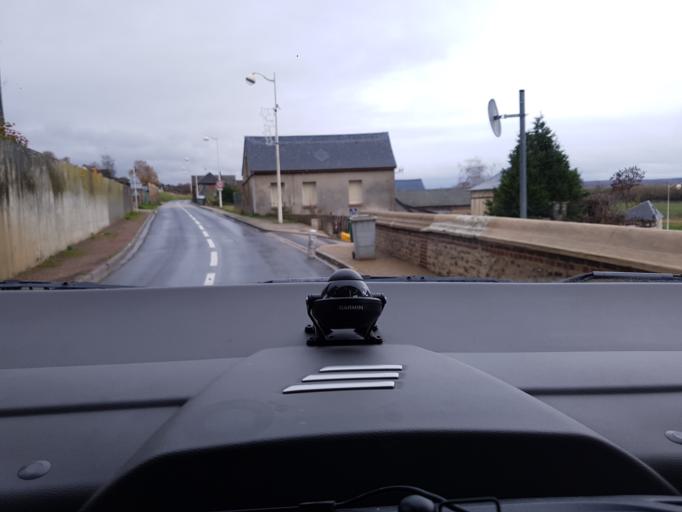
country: FR
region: Haute-Normandie
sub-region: Departement de la Seine-Maritime
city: Tourville-la-Riviere
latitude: 49.3199
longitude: 1.1253
